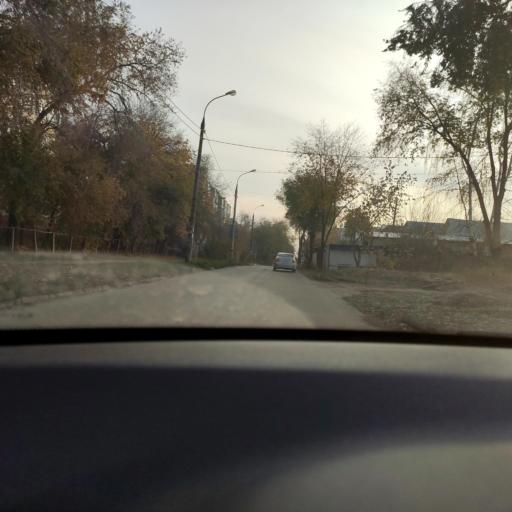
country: RU
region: Samara
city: Samara
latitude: 53.1851
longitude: 50.1964
